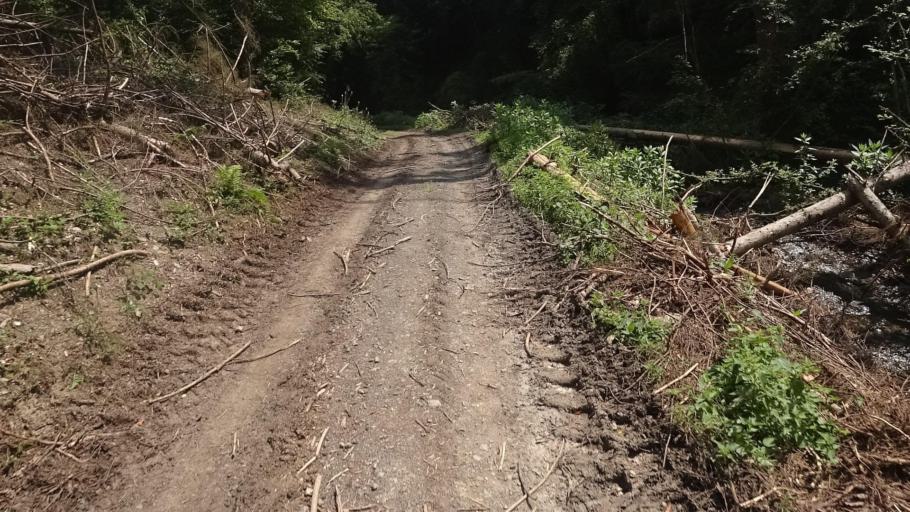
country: DE
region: Rheinland-Pfalz
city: Sankt Katharinen
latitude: 50.5853
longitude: 7.3896
